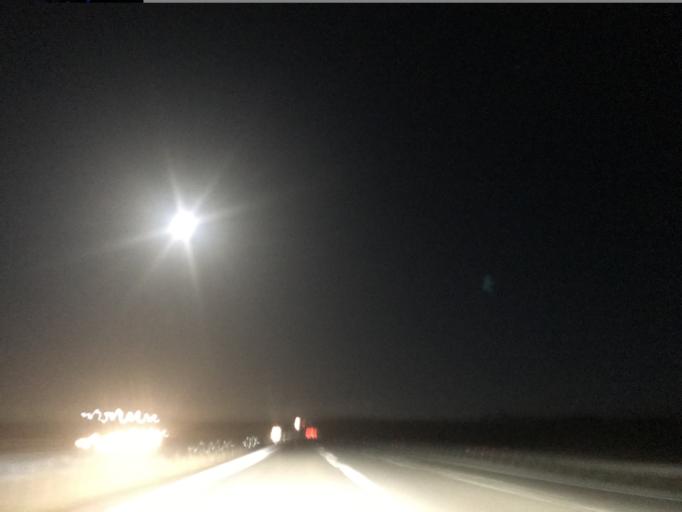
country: TR
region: Nigde
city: Ulukisla
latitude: 37.6391
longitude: 34.3903
